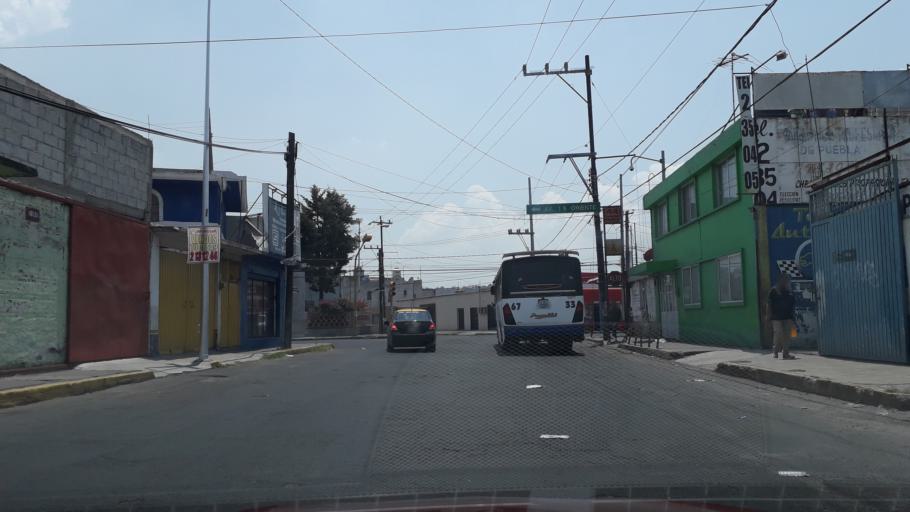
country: MX
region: Puebla
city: Puebla
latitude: 19.0474
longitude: -98.1651
